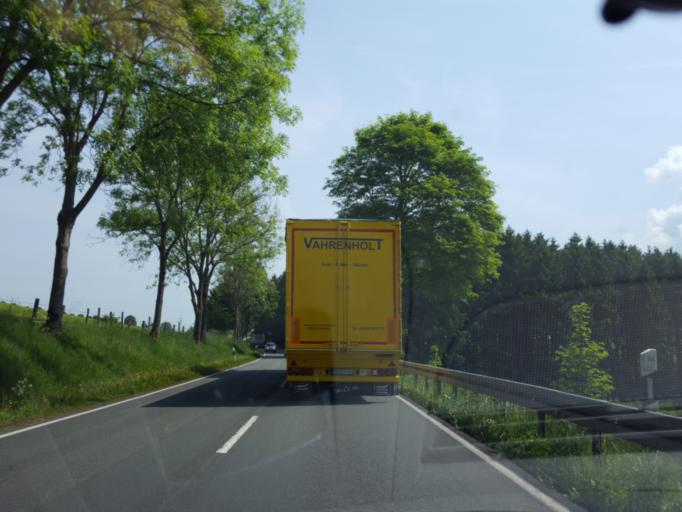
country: DE
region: North Rhine-Westphalia
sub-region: Regierungsbezirk Arnsberg
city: Olsberg
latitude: 51.3829
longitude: 8.4848
